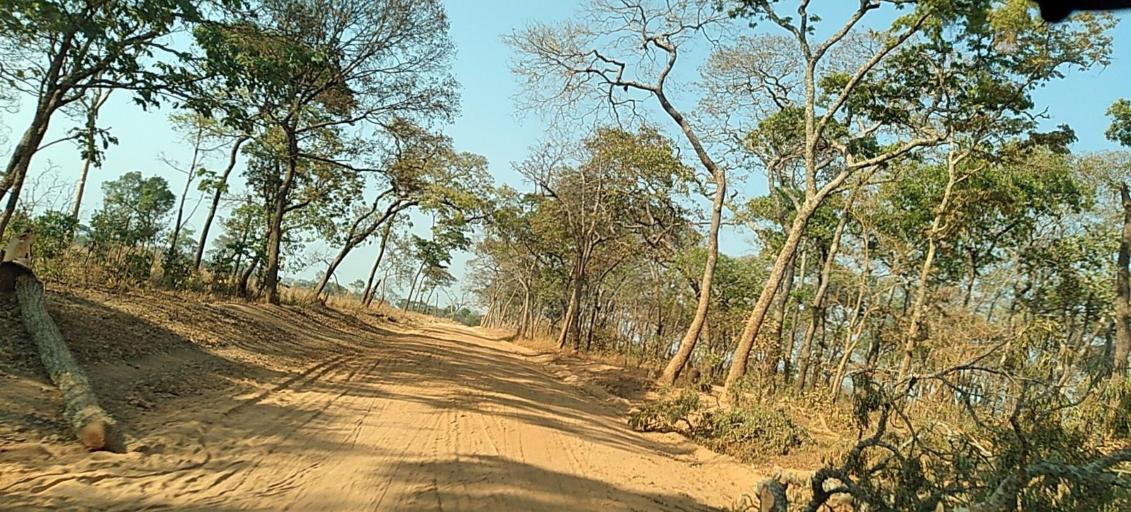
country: ZM
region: North-Western
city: Kasempa
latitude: -13.5686
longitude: 25.9951
